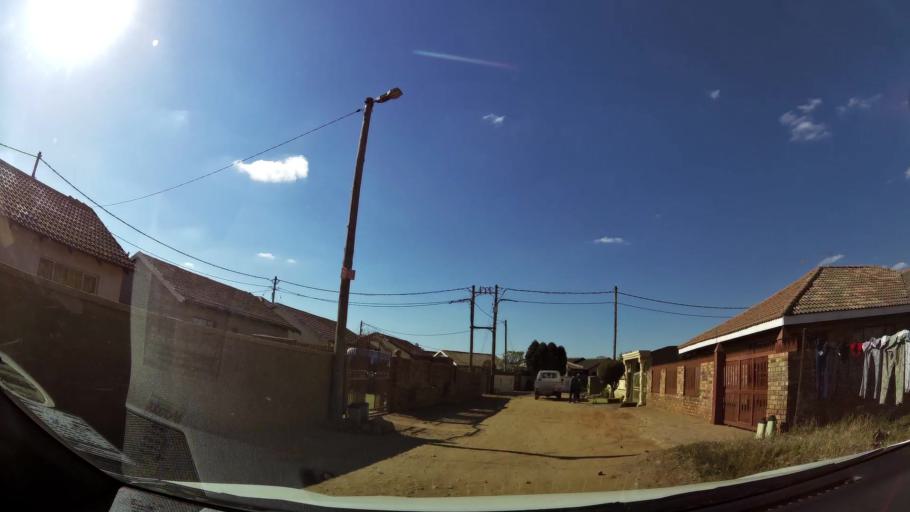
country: ZA
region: Gauteng
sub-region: City of Tshwane Metropolitan Municipality
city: Cullinan
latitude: -25.7130
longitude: 28.3923
